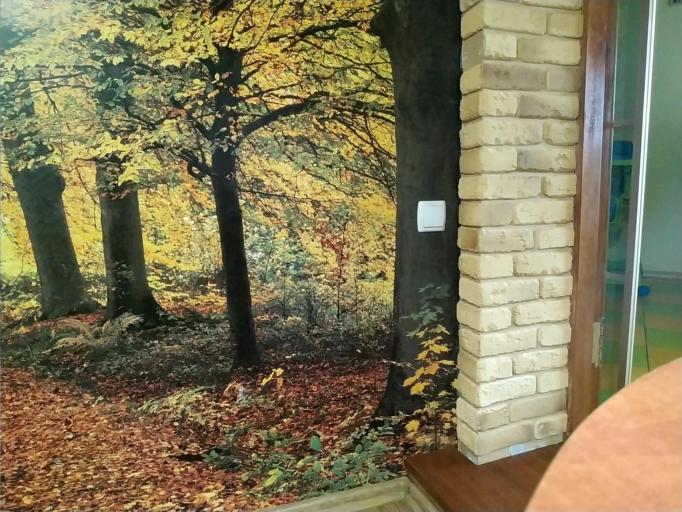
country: RU
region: Smolensk
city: Dorogobuzh
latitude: 54.9043
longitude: 33.3249
